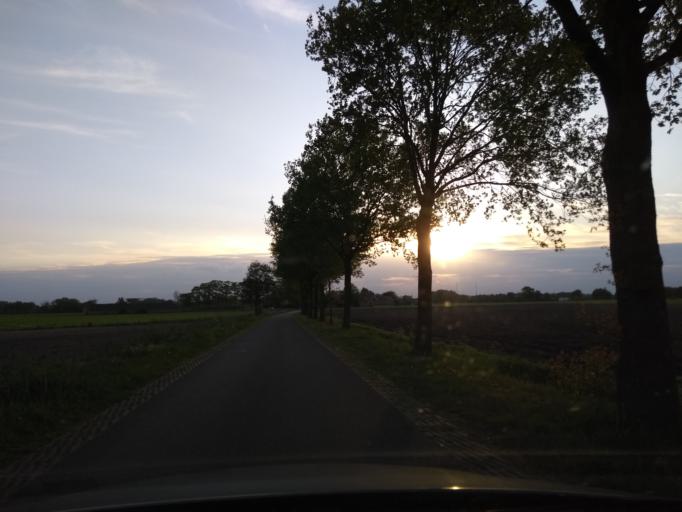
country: NL
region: Overijssel
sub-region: Gemeente Haaksbergen
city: Haaksbergen
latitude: 52.1732
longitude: 6.7286
